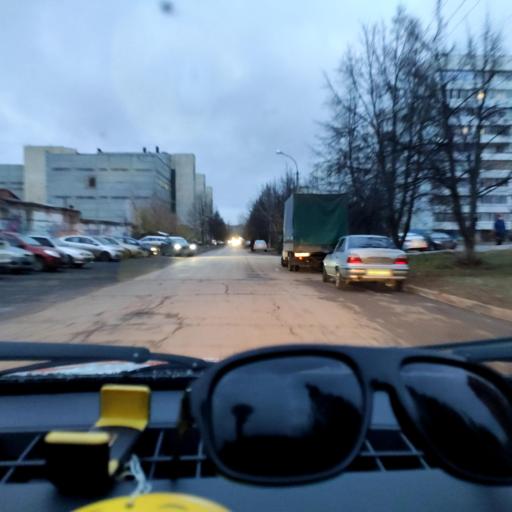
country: RU
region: Bashkortostan
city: Ufa
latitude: 54.7157
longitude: 56.0131
